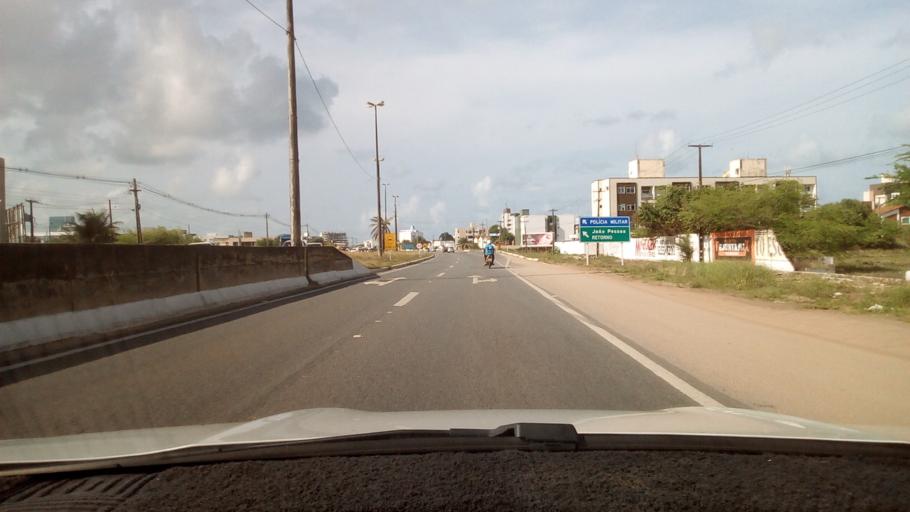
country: BR
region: Paraiba
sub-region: Cabedelo
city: Cabedelo
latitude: -7.0080
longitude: -34.8302
